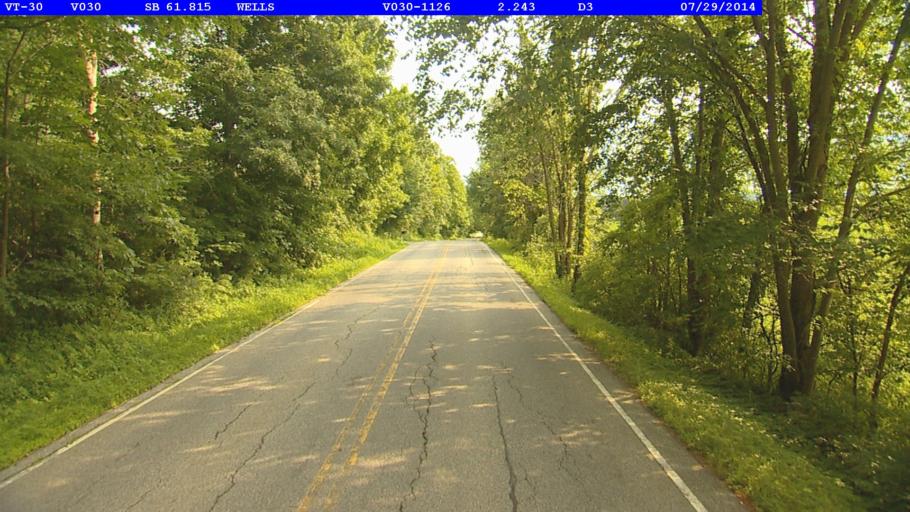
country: US
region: New York
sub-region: Washington County
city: Granville
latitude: 43.4267
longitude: -73.1968
